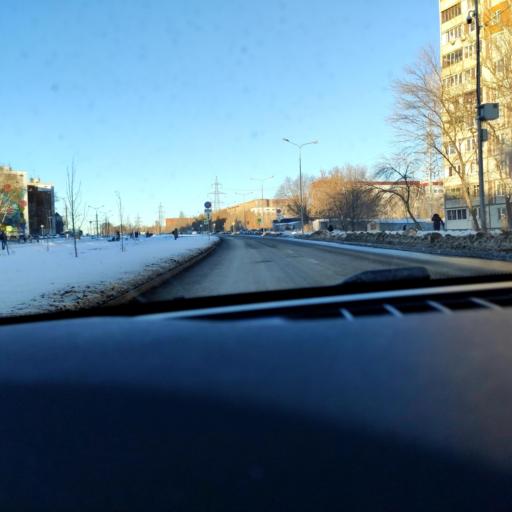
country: RU
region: Samara
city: Samara
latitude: 53.2585
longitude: 50.2467
